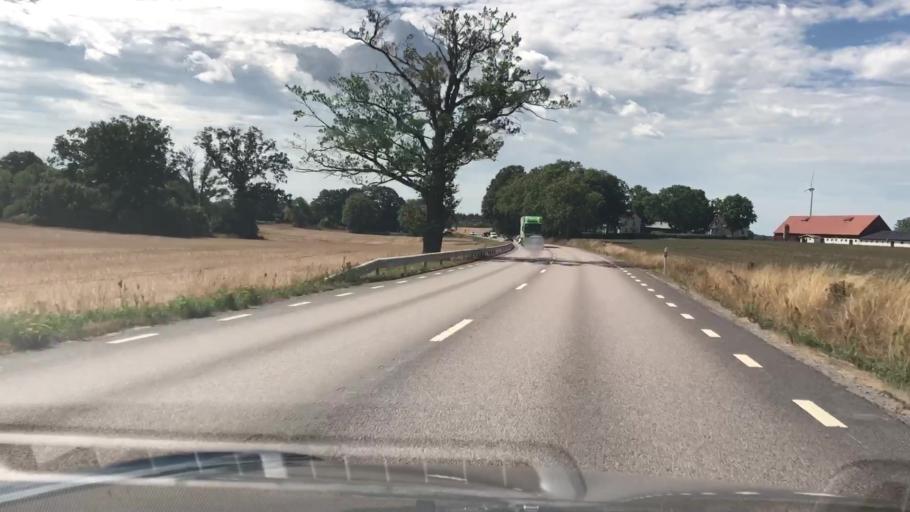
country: SE
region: Kalmar
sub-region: Torsas Kommun
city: Torsas
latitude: 56.4243
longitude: 16.0720
